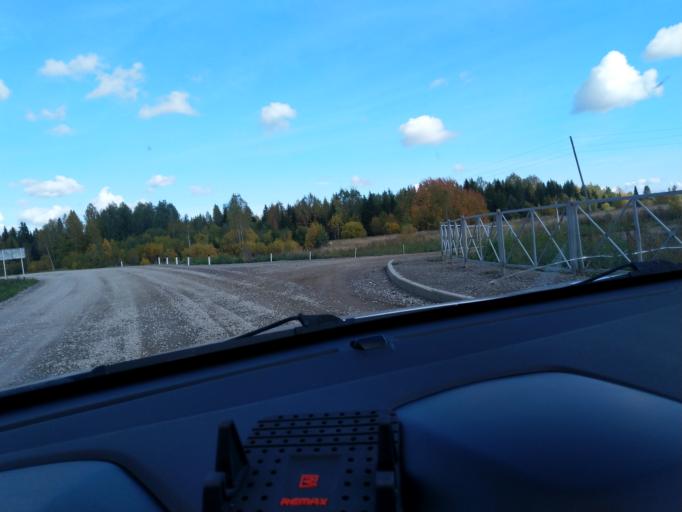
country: RU
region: Perm
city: Usol'ye
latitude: 59.4638
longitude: 56.3688
